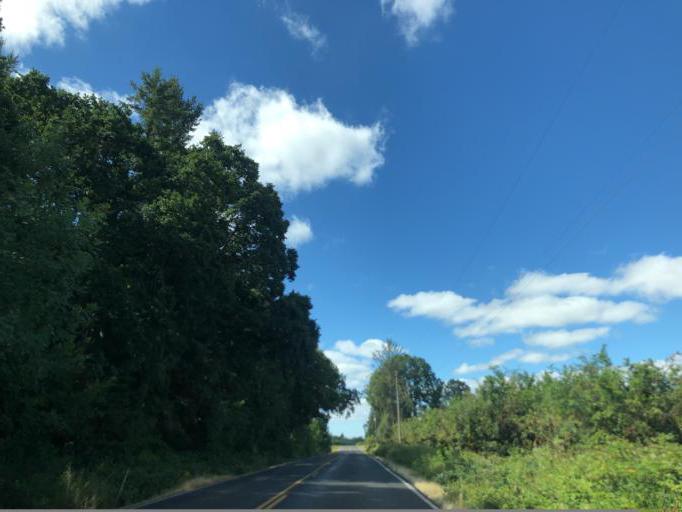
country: US
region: Oregon
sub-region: Marion County
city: Mount Angel
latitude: 45.1089
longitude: -122.7281
